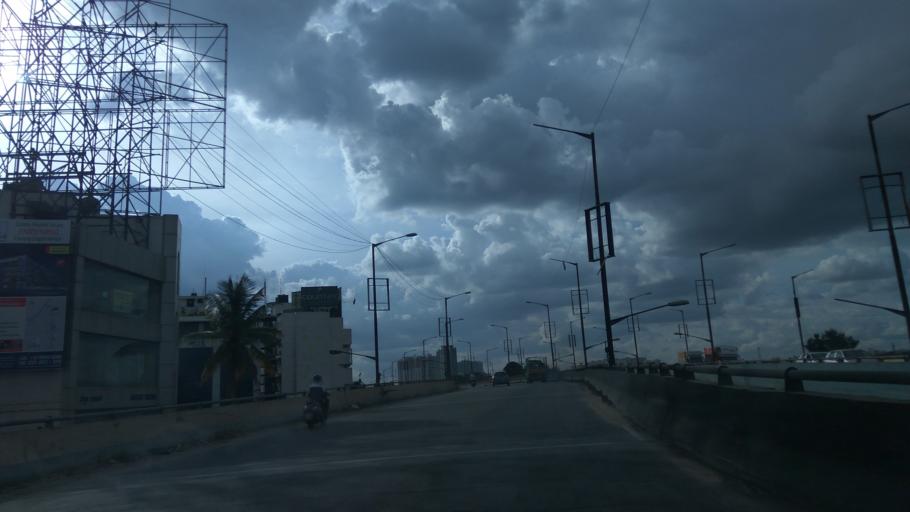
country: IN
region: Karnataka
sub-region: Bangalore Urban
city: Yelahanka
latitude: 13.0416
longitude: 77.6145
